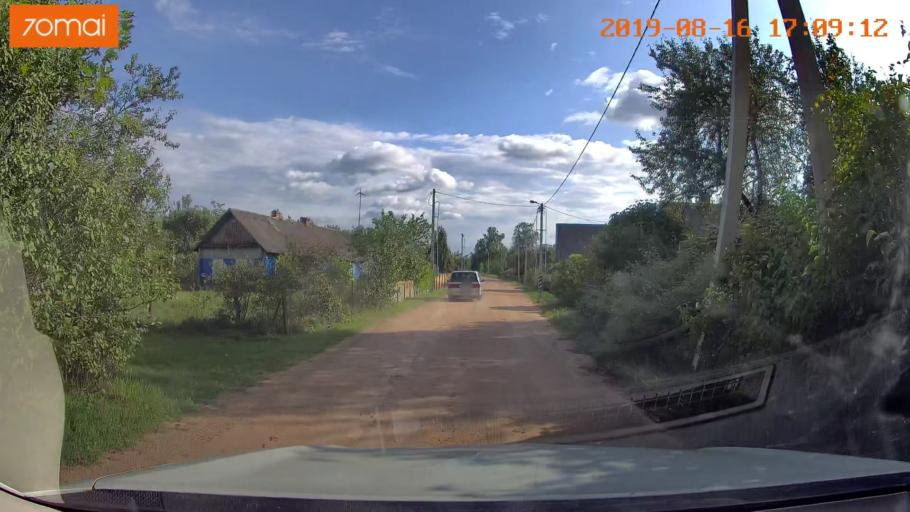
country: BY
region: Mogilev
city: Hlusha
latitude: 53.2155
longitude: 28.9253
